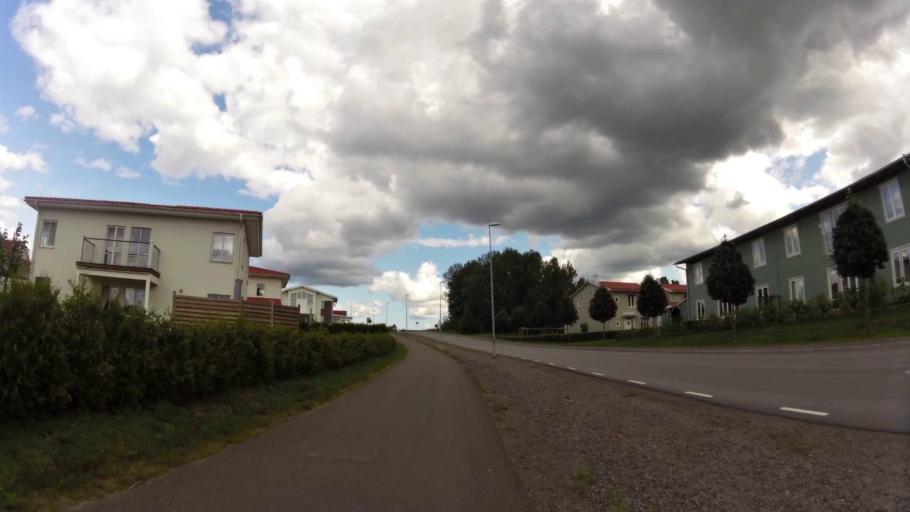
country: SE
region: OEstergoetland
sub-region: Linkopings Kommun
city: Ekangen
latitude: 58.4331
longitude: 15.7004
